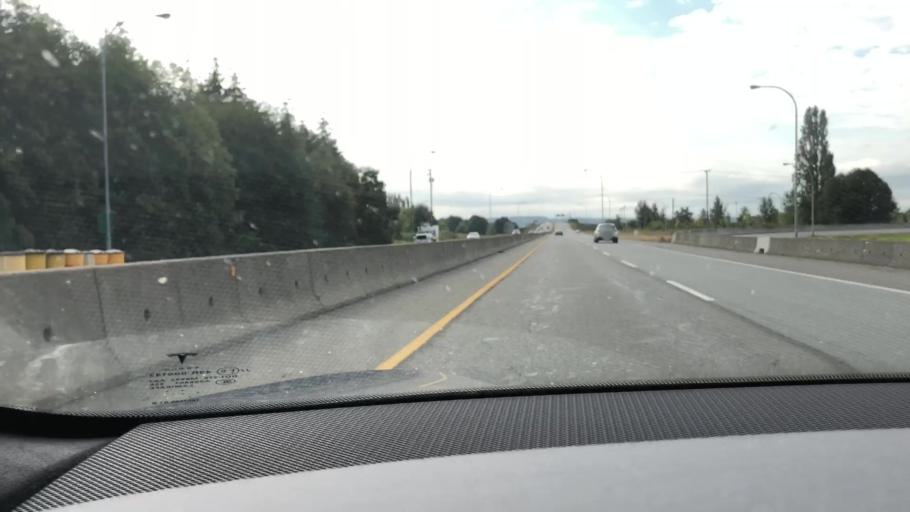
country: CA
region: British Columbia
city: Delta
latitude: 49.1016
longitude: -122.9000
